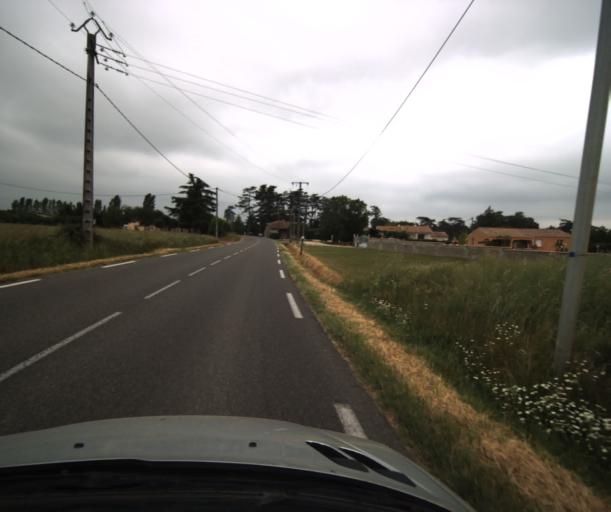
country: FR
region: Midi-Pyrenees
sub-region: Departement du Tarn-et-Garonne
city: Saint-Nicolas-de-la-Grave
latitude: 44.0429
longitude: 1.0345
